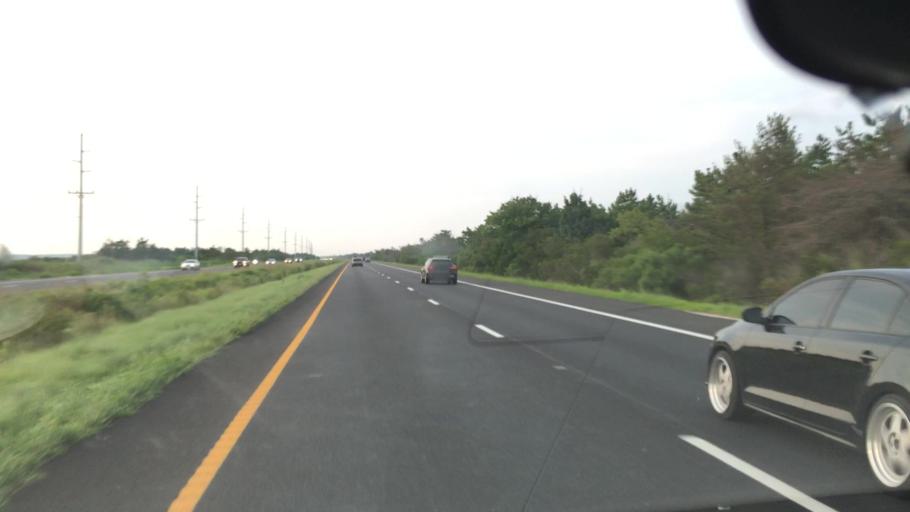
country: US
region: Delaware
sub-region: Sussex County
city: Rehoboth Beach
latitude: 38.6426
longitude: -75.0683
